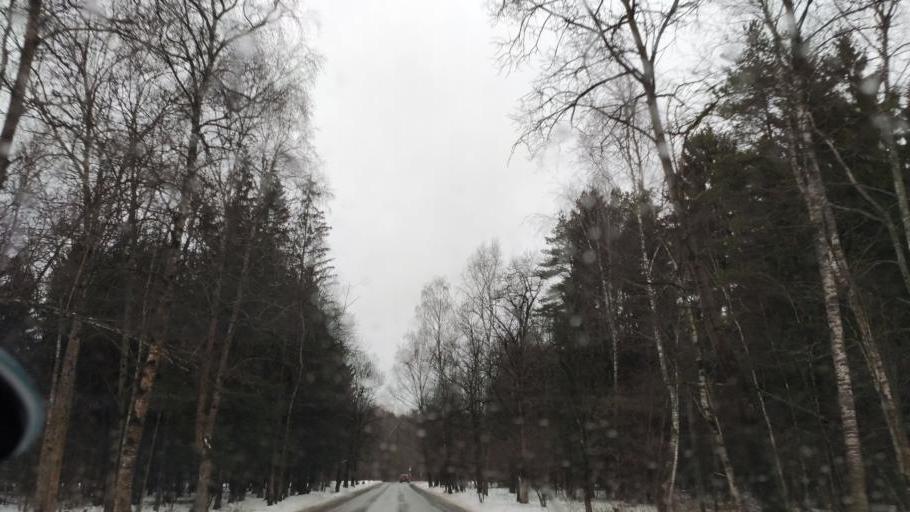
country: RU
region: Moskovskaya
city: Vatutinki
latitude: 55.4806
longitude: 37.3362
